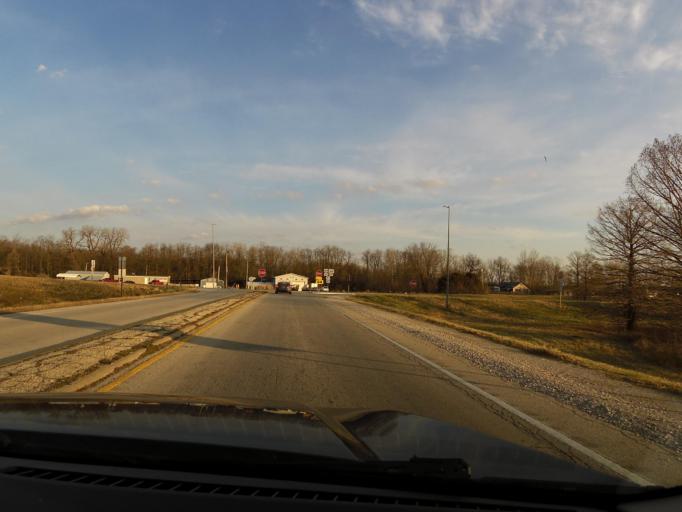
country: US
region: Illinois
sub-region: Fayette County
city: Vandalia
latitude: 38.9594
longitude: -89.0848
